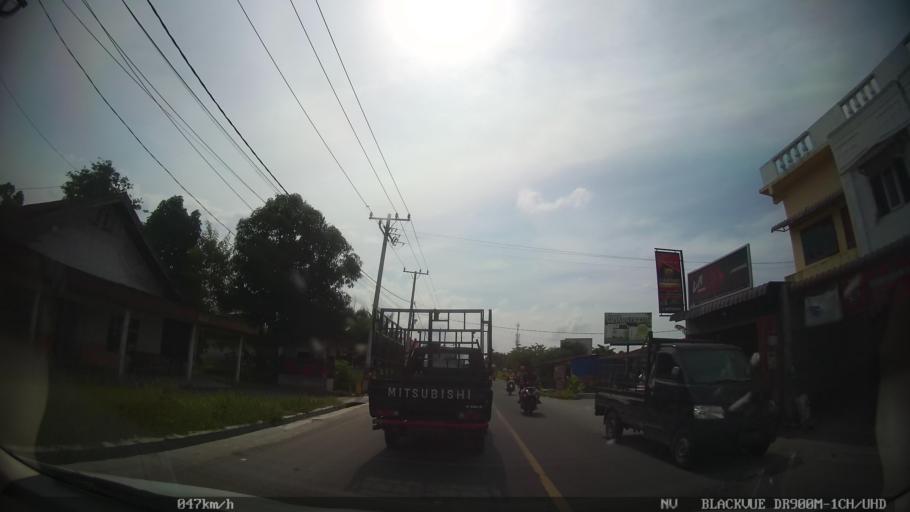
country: ID
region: North Sumatra
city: Percut
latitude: 3.6116
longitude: 98.8202
